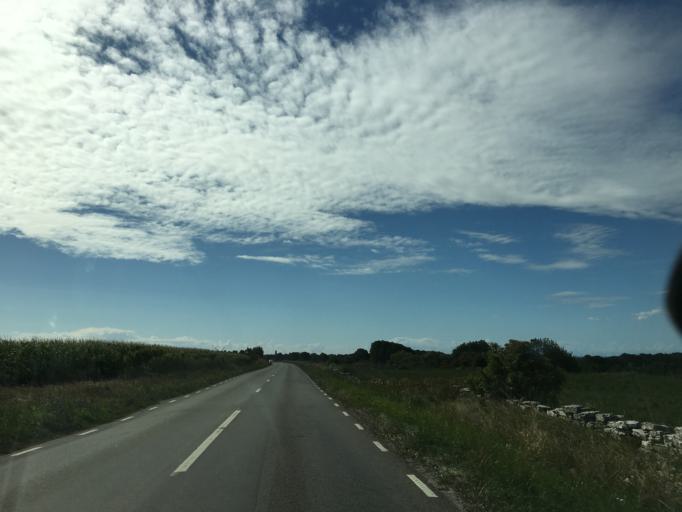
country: SE
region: Kalmar
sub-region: Morbylanga Kommun
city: Moerbylanga
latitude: 56.4769
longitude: 16.4295
